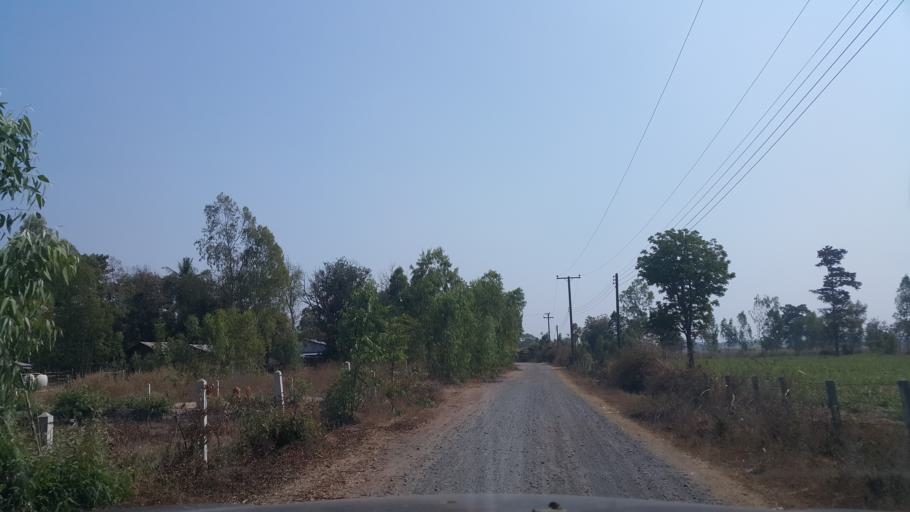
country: TH
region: Buriram
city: Krasang
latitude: 15.1076
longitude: 103.3778
